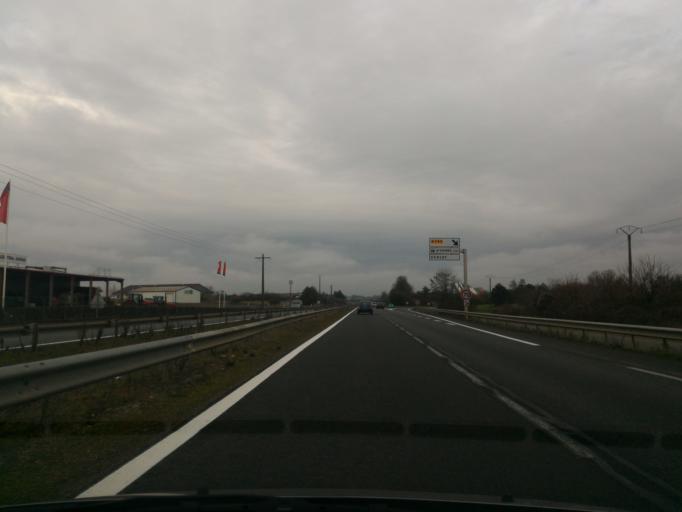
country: FR
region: Poitou-Charentes
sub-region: Departement de la Vienne
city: Vivonne
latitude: 46.4184
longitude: 0.2495
